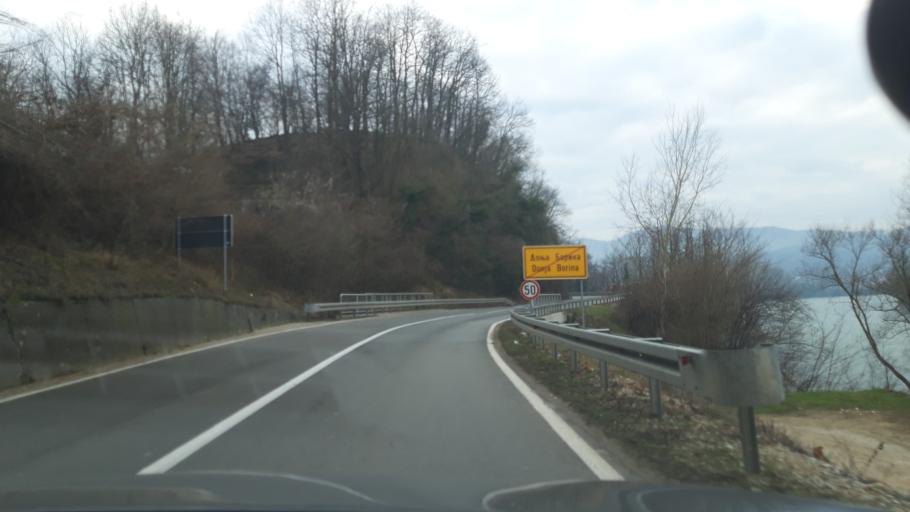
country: BA
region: Republika Srpska
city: Zvornik
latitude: 44.4173
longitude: 19.1481
